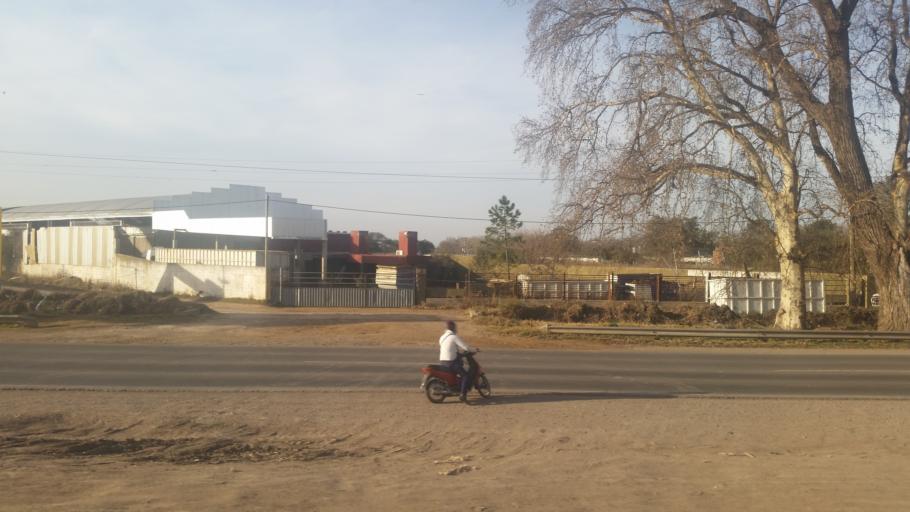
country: AR
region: Cordoba
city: Toledo
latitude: -31.4865
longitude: -64.0807
